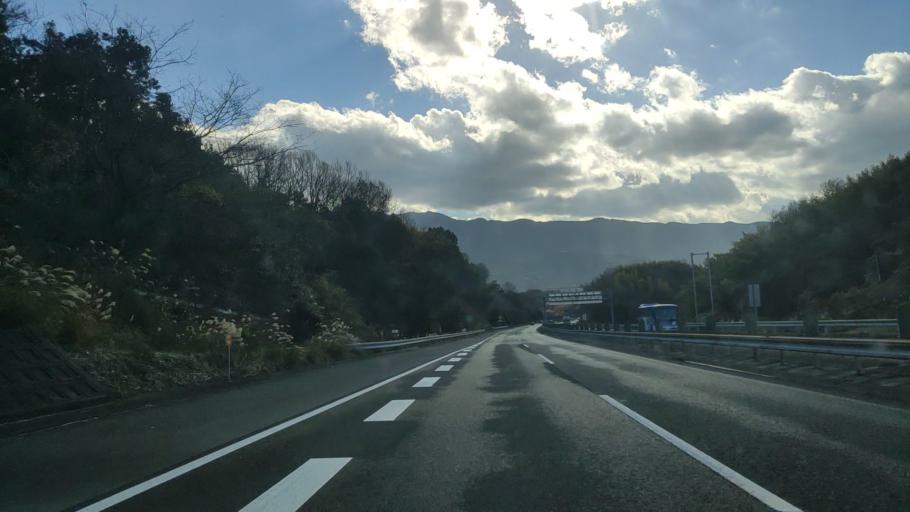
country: JP
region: Ehime
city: Kawanoecho
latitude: 33.9968
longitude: 133.5962
